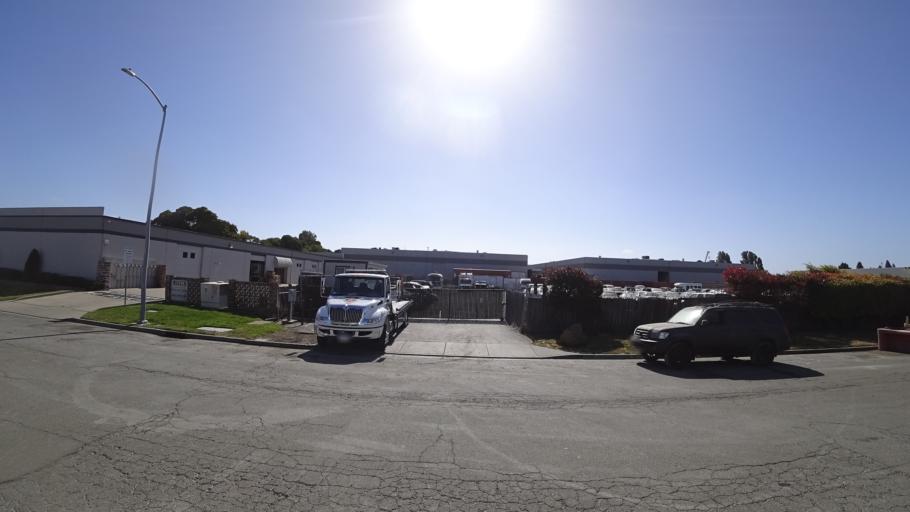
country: US
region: California
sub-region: Alameda County
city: San Lorenzo
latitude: 37.6404
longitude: -122.1295
